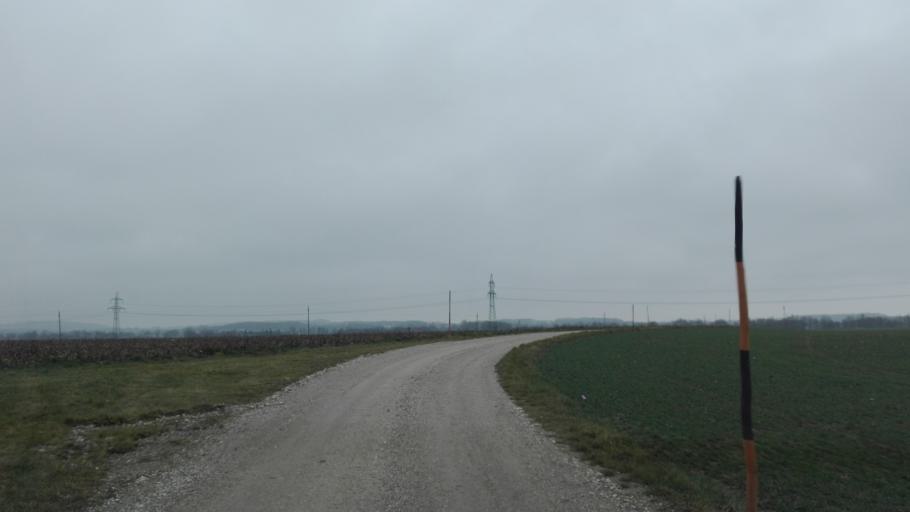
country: AT
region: Upper Austria
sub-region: Politischer Bezirk Linz-Land
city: Horsching
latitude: 48.2139
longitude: 14.1437
